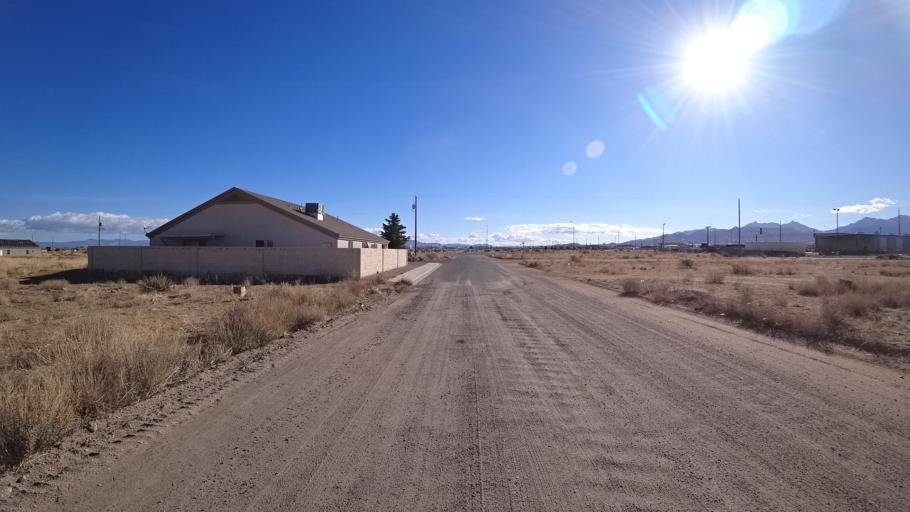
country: US
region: Arizona
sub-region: Mohave County
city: New Kingman-Butler
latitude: 35.2267
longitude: -114.0130
